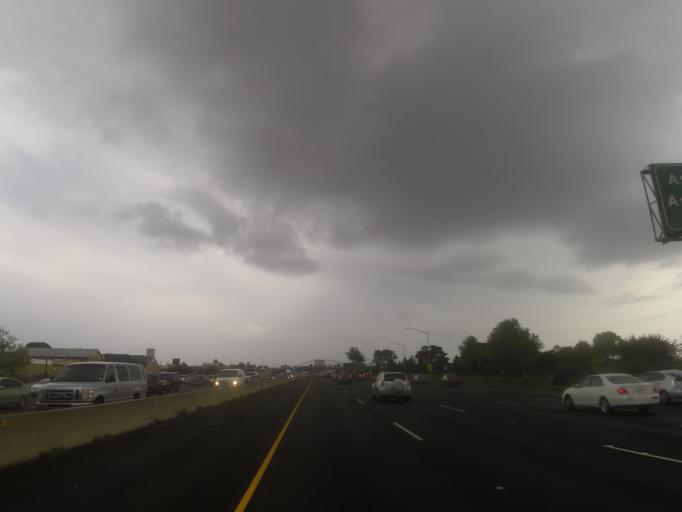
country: US
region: California
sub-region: Alameda County
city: Albany
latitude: 37.8702
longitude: -122.3049
